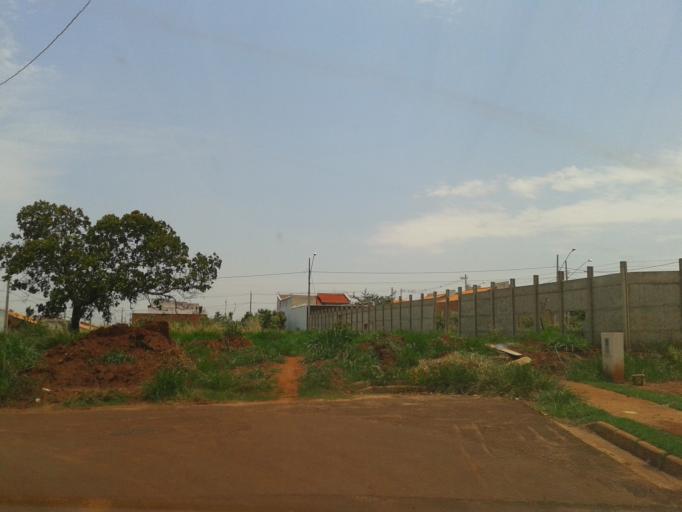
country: BR
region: Minas Gerais
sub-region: Ituiutaba
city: Ituiutaba
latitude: -18.9878
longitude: -49.4364
